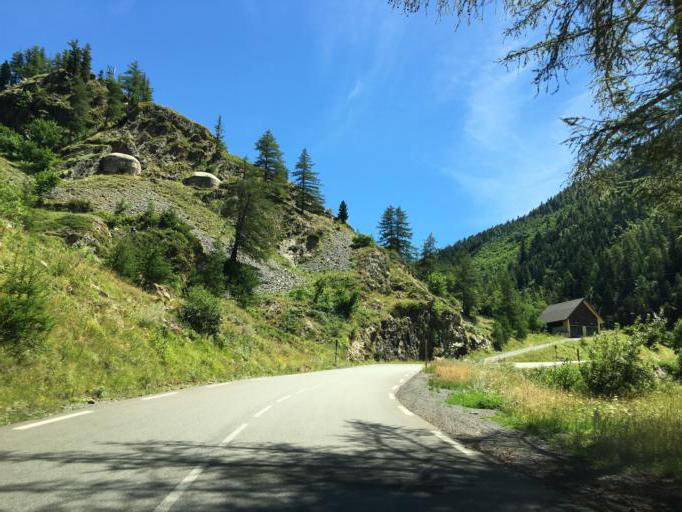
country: IT
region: Piedmont
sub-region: Provincia di Cuneo
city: Vinadio
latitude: 44.2087
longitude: 7.1077
